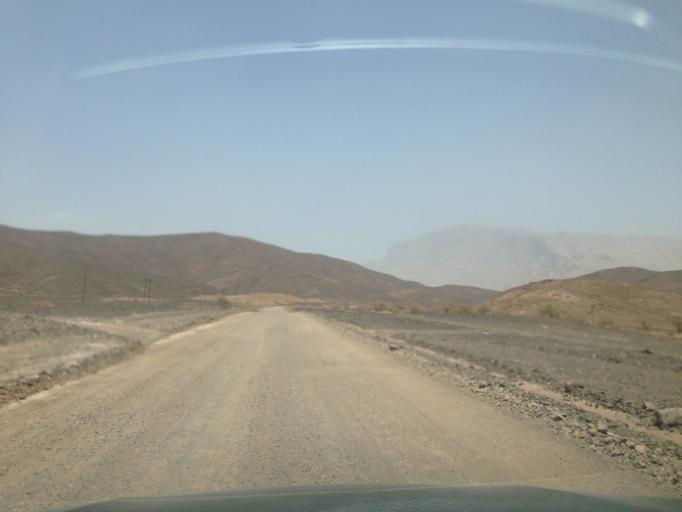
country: OM
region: Az Zahirah
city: `Ibri
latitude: 23.2004
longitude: 56.8733
